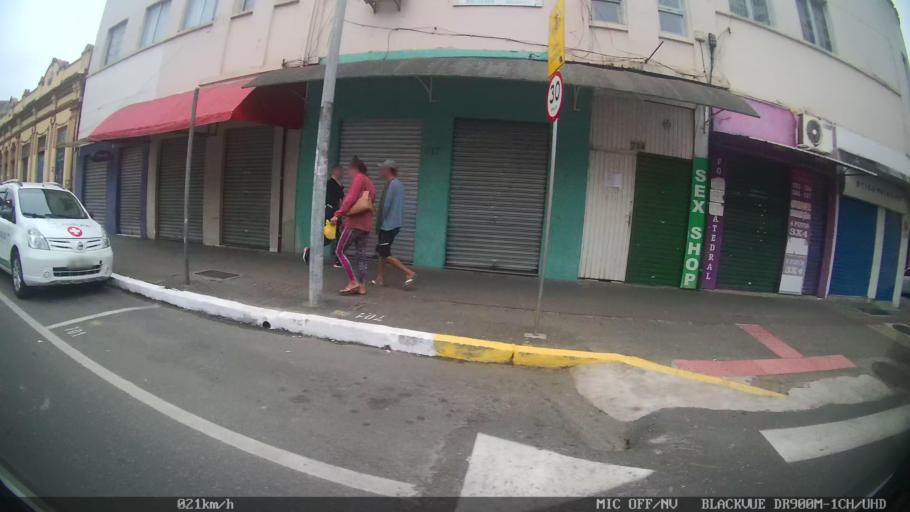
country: BR
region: Santa Catarina
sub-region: Joinville
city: Joinville
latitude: -26.3055
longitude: -48.8451
